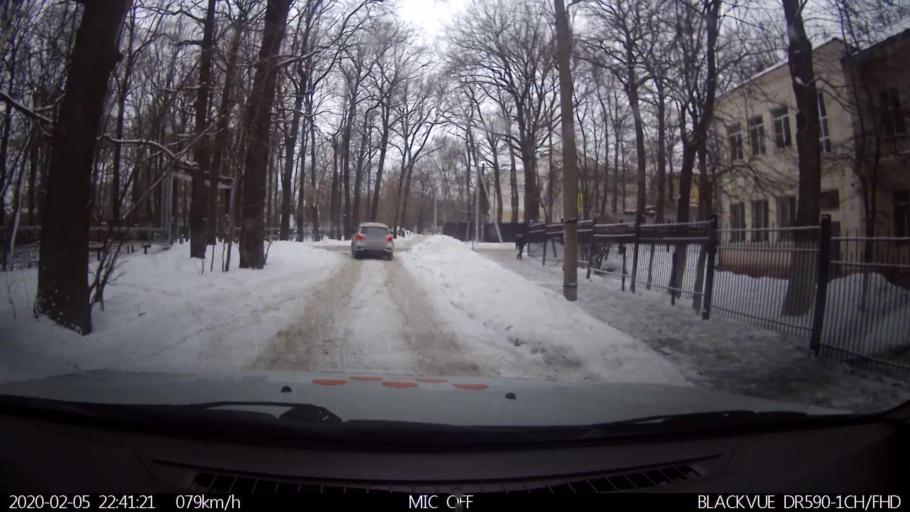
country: RU
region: Nizjnij Novgorod
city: Imeni Stepana Razina
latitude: 54.7211
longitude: 44.3369
